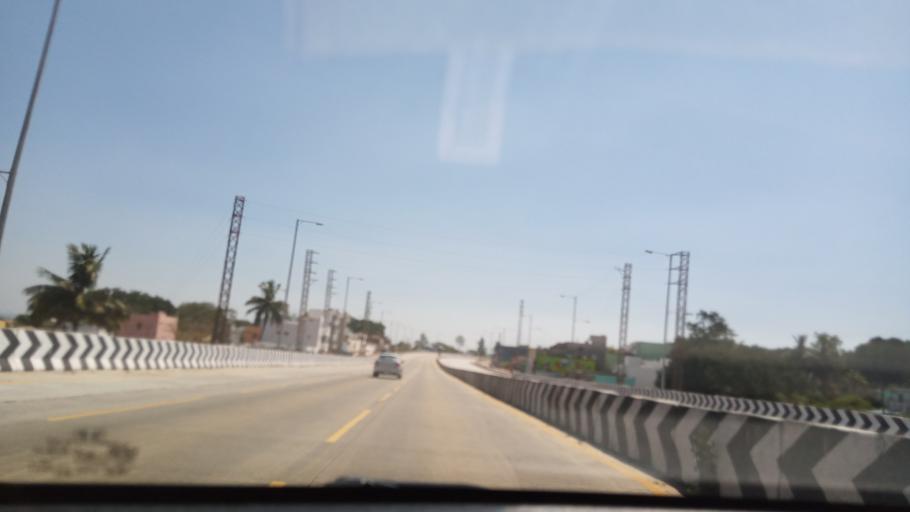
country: IN
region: Andhra Pradesh
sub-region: Chittoor
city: Palmaner
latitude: 13.1830
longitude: 78.6383
